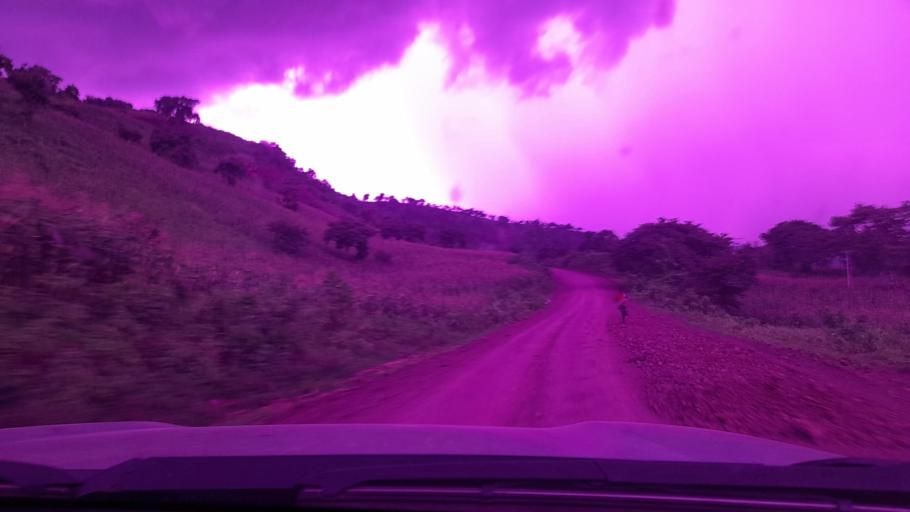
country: ET
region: Southern Nations, Nationalities, and People's Region
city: Mizan Teferi
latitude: 6.7299
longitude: 35.8649
